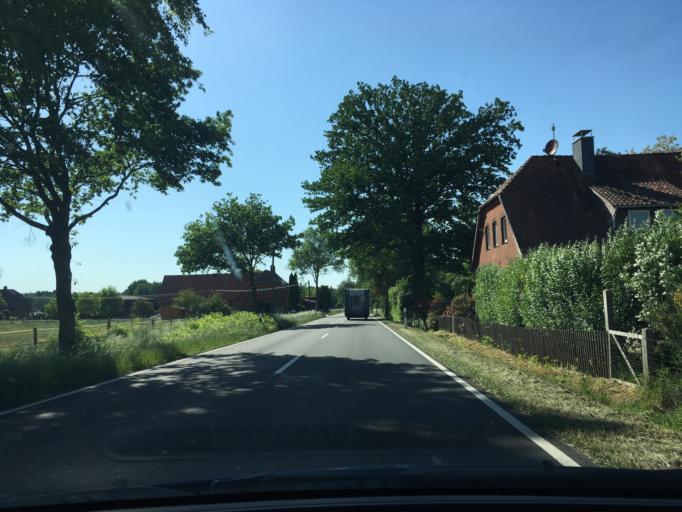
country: DE
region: Lower Saxony
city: Bad Fallingbostel
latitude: 52.9074
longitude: 9.7340
